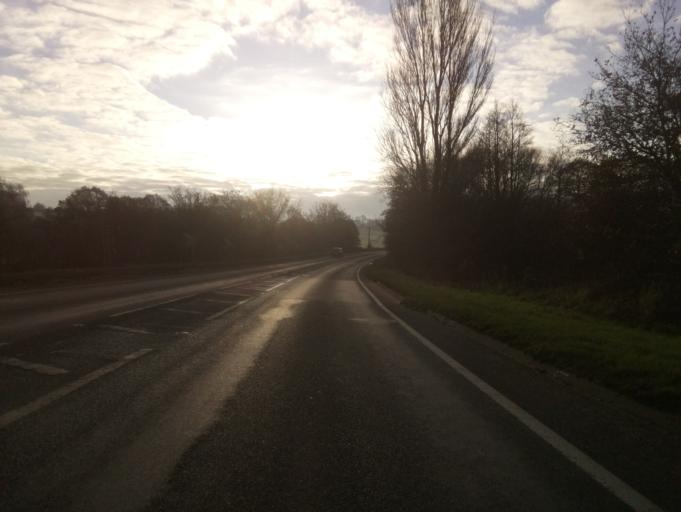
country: GB
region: England
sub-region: Warwickshire
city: Curdworth
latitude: 52.5717
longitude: -1.7641
